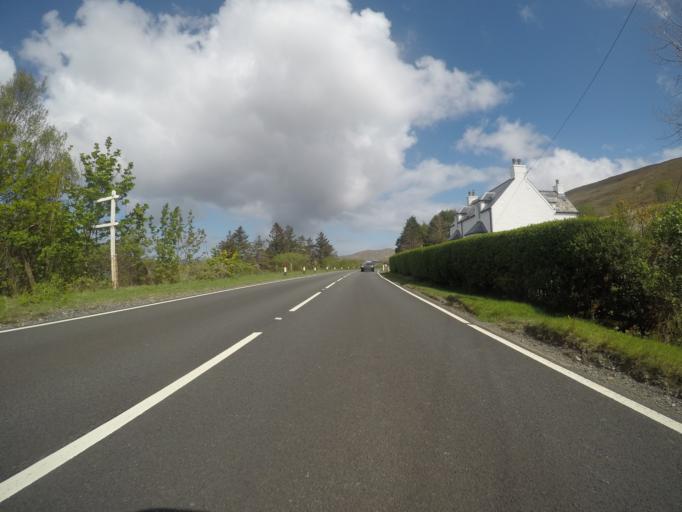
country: GB
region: Scotland
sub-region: Highland
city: Portree
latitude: 57.2786
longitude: -6.0403
